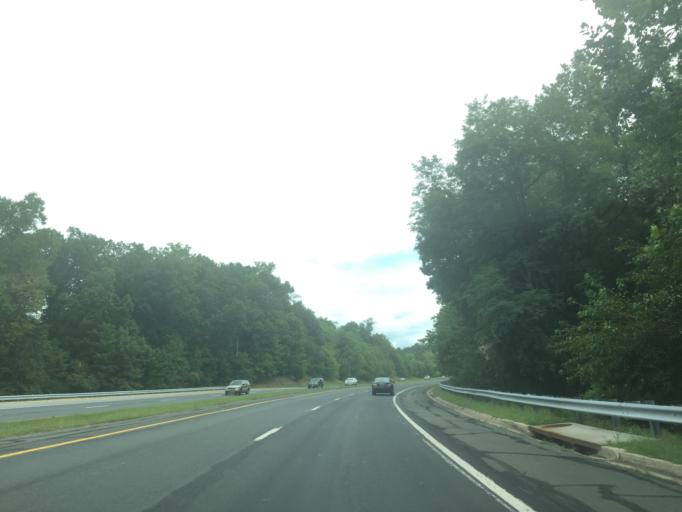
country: US
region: Maryland
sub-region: Montgomery County
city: Gaithersburg
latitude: 39.1567
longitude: -77.1838
